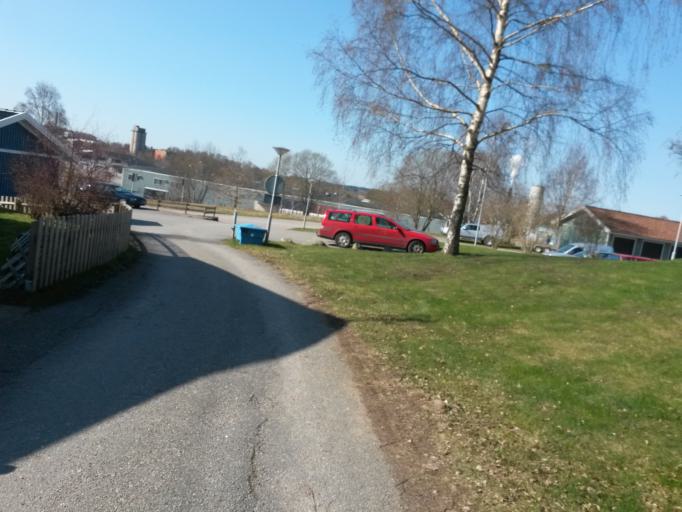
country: SE
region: Vaestra Goetaland
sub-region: Vargarda Kommun
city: Vargarda
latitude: 58.0263
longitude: 12.7974
